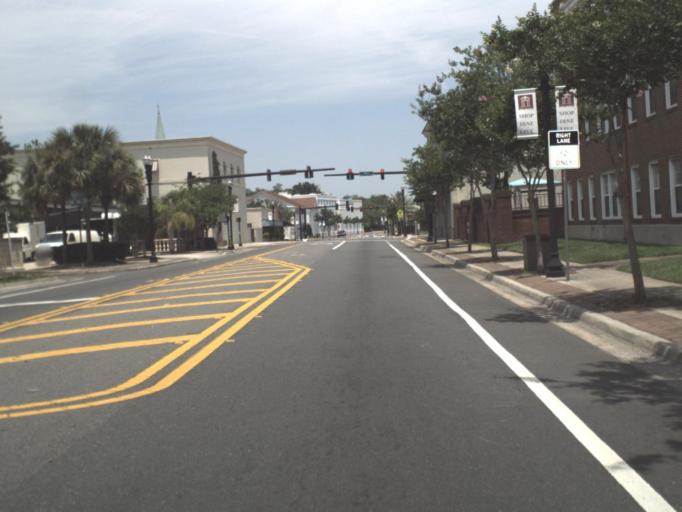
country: US
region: Florida
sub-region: Duval County
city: Jacksonville
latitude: 30.3033
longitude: -81.6520
